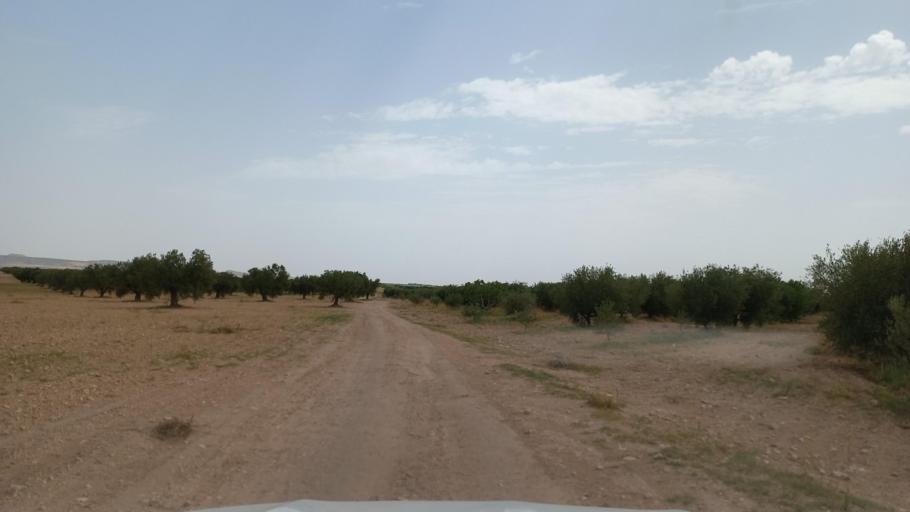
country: TN
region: Al Qasrayn
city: Kasserine
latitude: 35.2895
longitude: 9.0252
